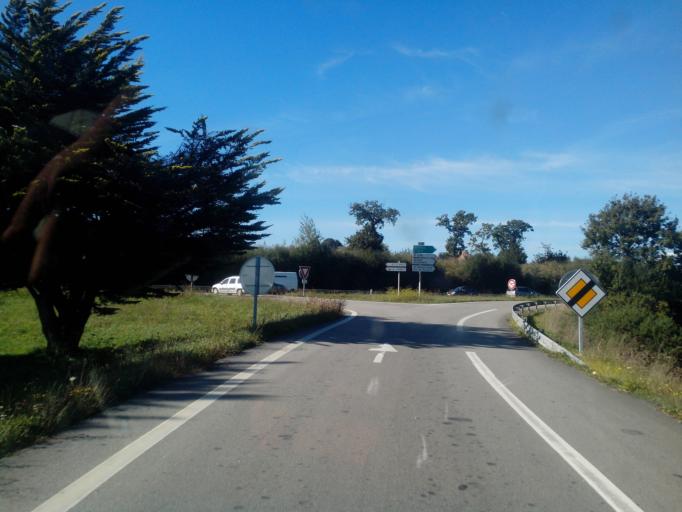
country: FR
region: Brittany
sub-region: Departement du Morbihan
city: Vannes
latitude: 47.6669
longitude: -2.7246
